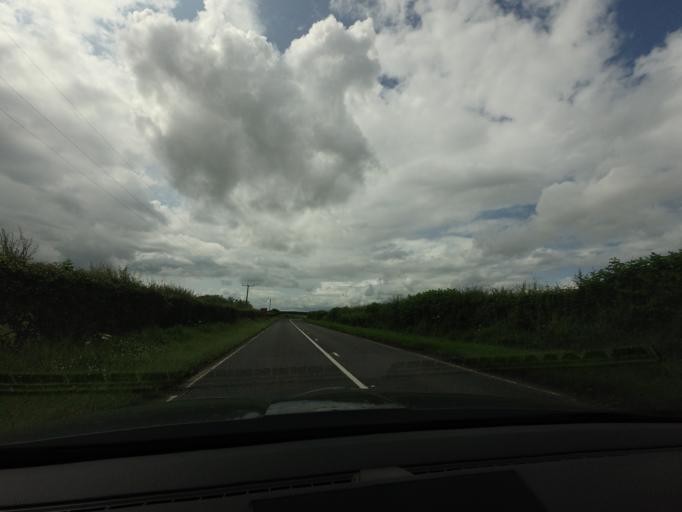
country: GB
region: Scotland
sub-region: Aberdeenshire
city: Whitehills
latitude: 57.6532
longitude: -2.6176
